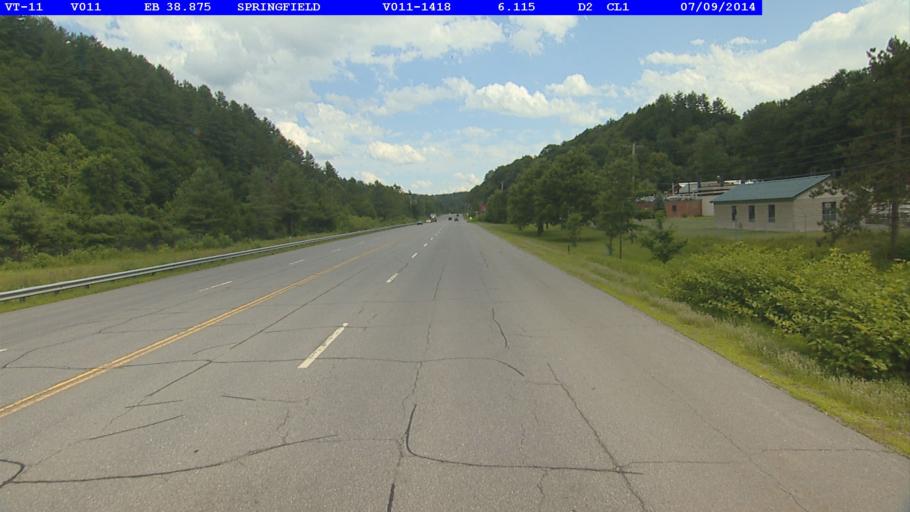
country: US
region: Vermont
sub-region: Windsor County
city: Springfield
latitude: 43.2807
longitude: -72.4695
